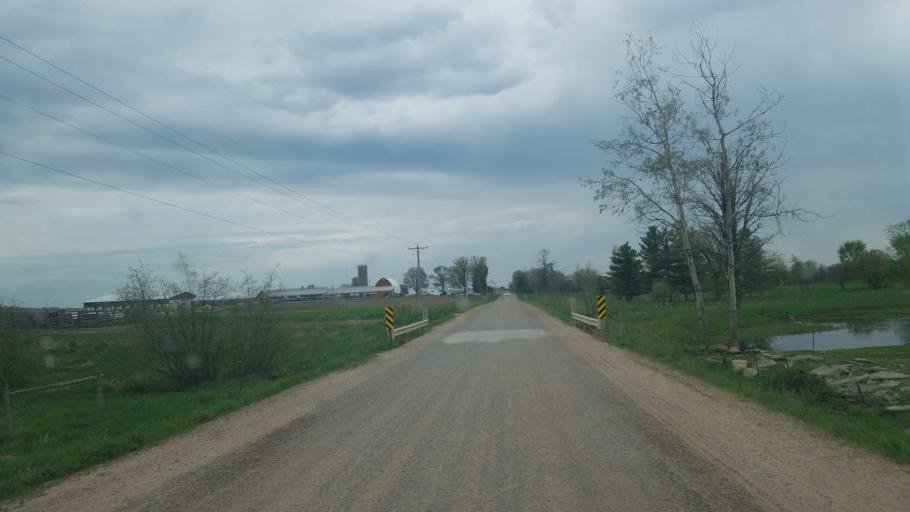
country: US
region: Wisconsin
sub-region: Clark County
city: Loyal
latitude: 44.6371
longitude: -90.4565
